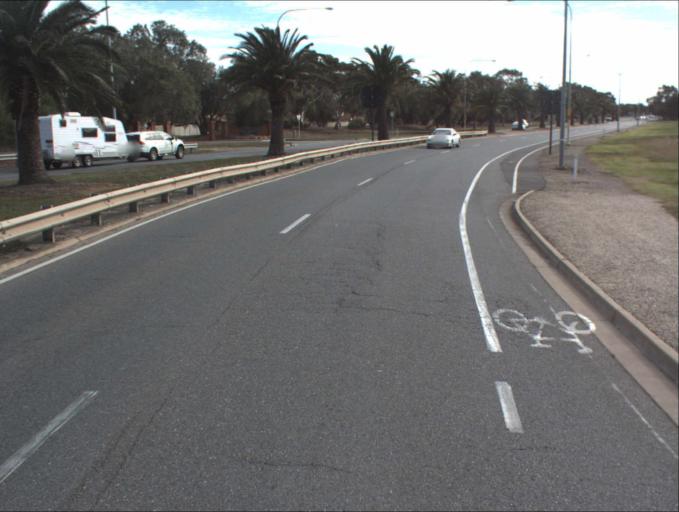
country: AU
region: South Australia
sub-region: Charles Sturt
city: West Lakes Shore
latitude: -34.8586
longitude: 138.5028
